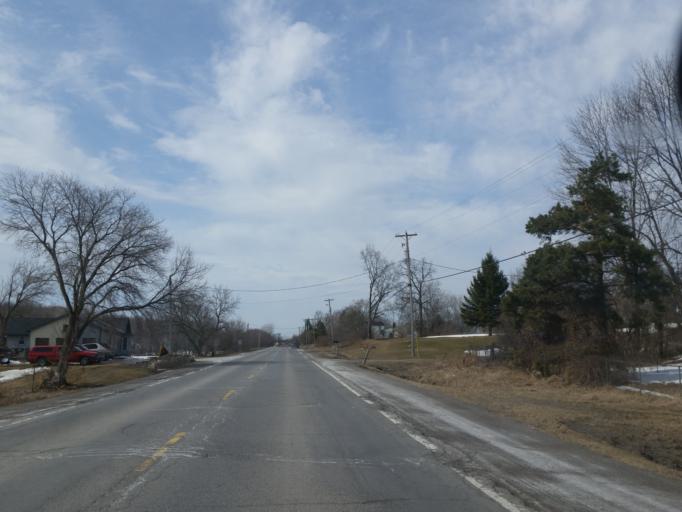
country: CA
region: Ontario
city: Deseronto
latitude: 44.1939
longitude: -77.1004
